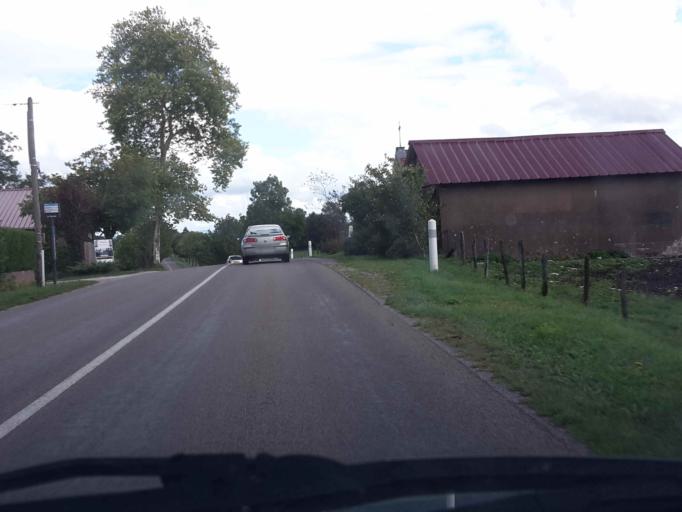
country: FR
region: Franche-Comte
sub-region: Departement du Doubs
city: Nancray
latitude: 47.2427
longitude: 6.1475
